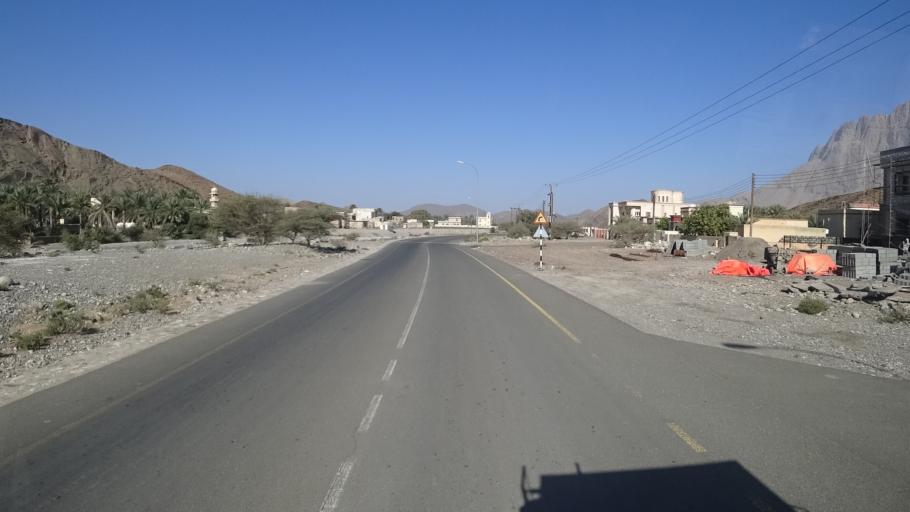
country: OM
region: Muhafazat ad Dakhiliyah
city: Bahla'
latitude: 23.2150
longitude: 57.0171
